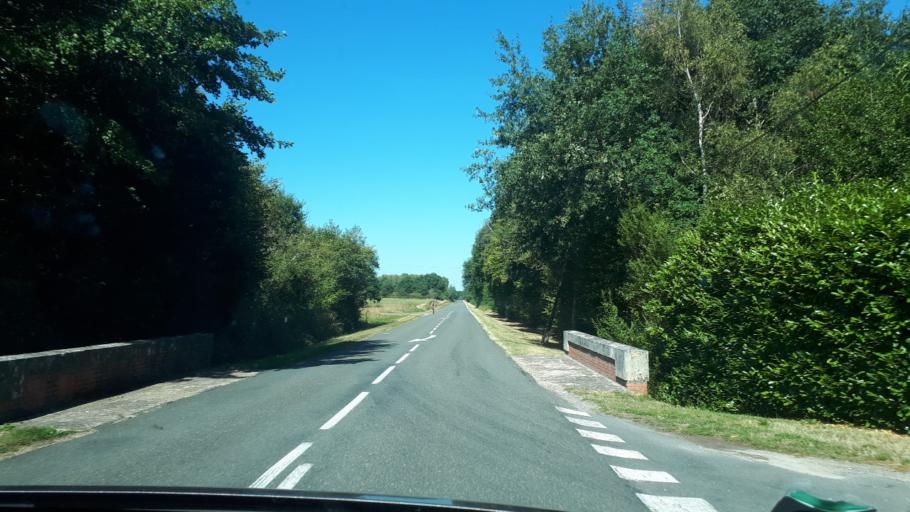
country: FR
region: Centre
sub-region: Departement du Loiret
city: Cerdon
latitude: 47.6373
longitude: 2.4176
